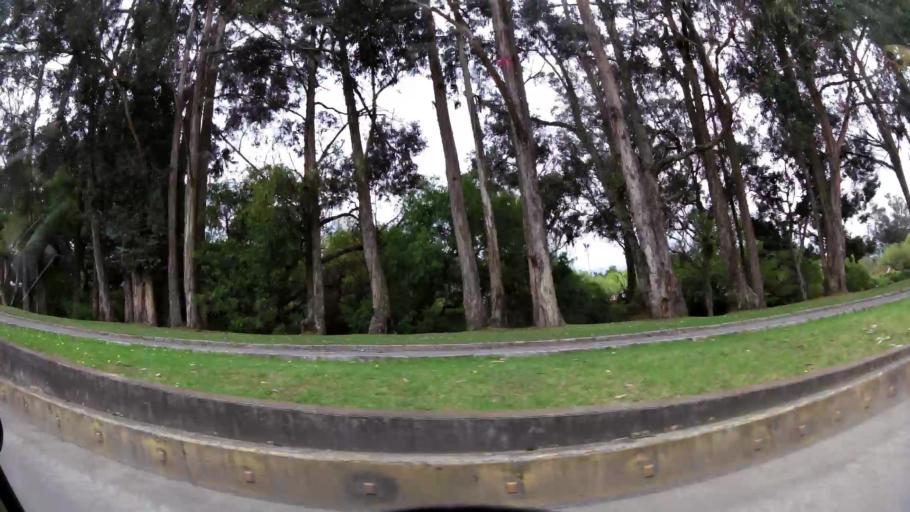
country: EC
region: Azuay
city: Cuenca
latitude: -2.9129
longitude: -78.9892
